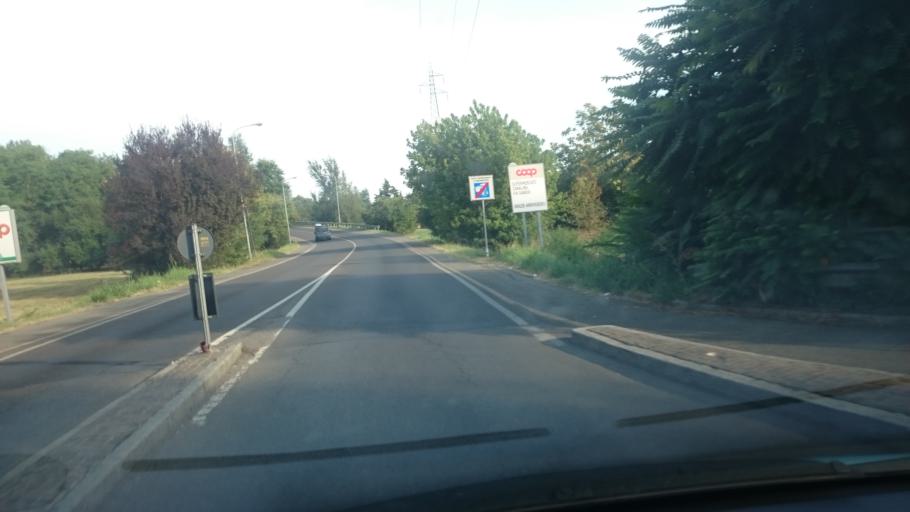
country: IT
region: Emilia-Romagna
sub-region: Provincia di Reggio Emilia
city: Reggio nell'Emilia
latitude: 44.6773
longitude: 10.6231
